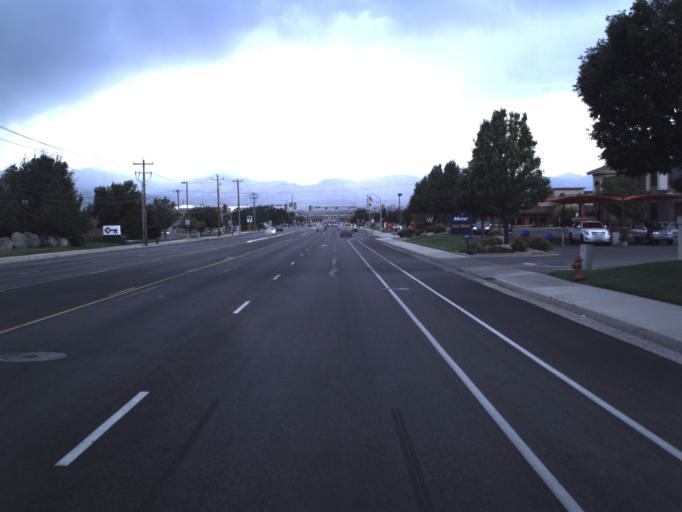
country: US
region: Utah
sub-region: Salt Lake County
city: Draper
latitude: 40.5268
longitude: -111.8790
